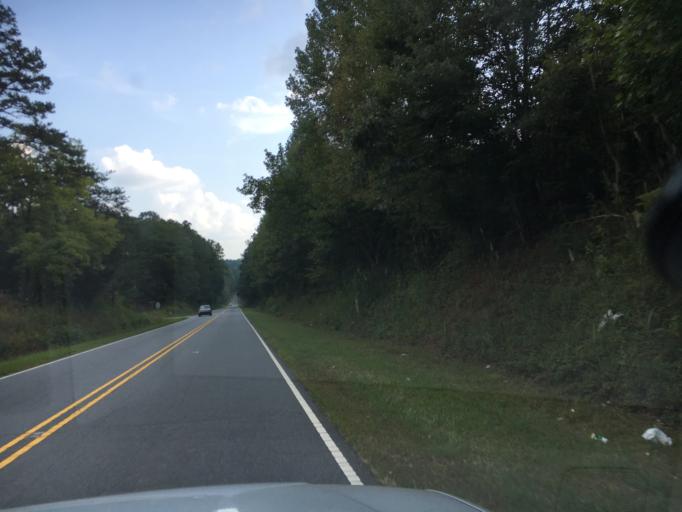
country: US
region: North Carolina
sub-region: Rutherford County
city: Rutherfordton
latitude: 35.4640
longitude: -81.9800
